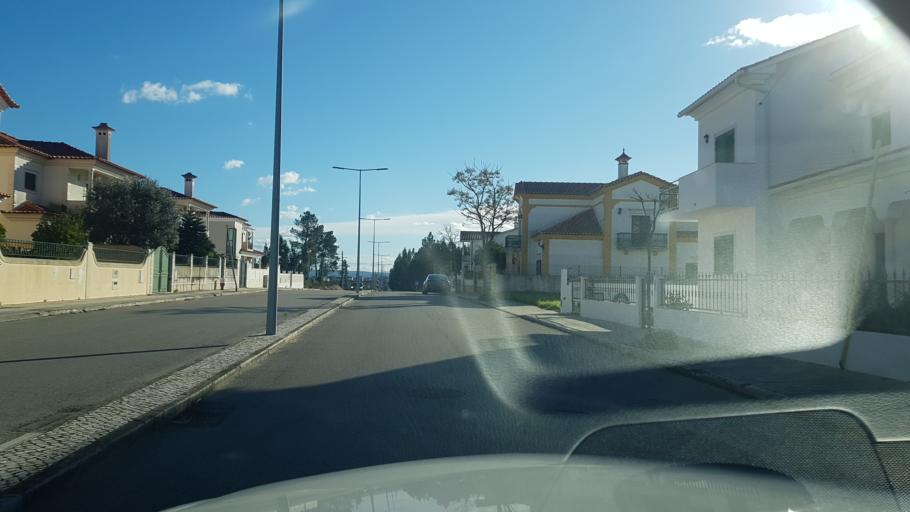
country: PT
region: Santarem
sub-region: Entroncamento
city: Entroncamento
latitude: 39.4787
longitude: -8.4686
